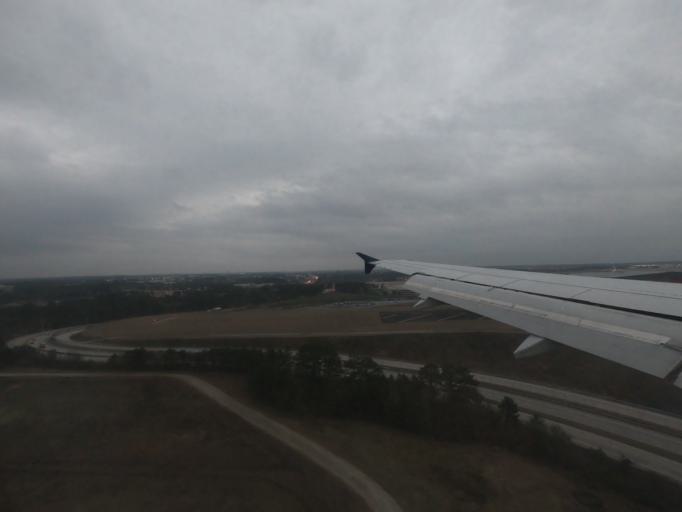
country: US
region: Georgia
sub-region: Fulton County
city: Hapeville
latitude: 33.6494
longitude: -84.4042
